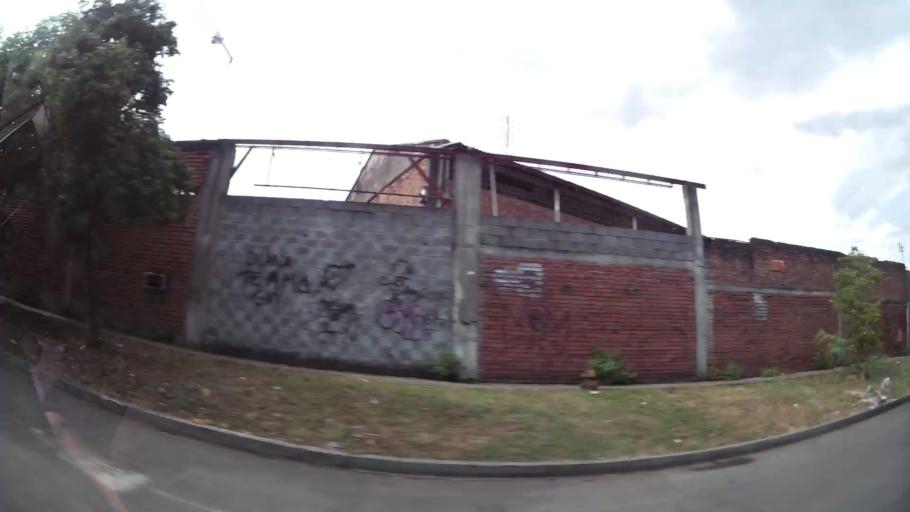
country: CO
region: Valle del Cauca
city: Cali
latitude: 3.4713
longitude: -76.5043
